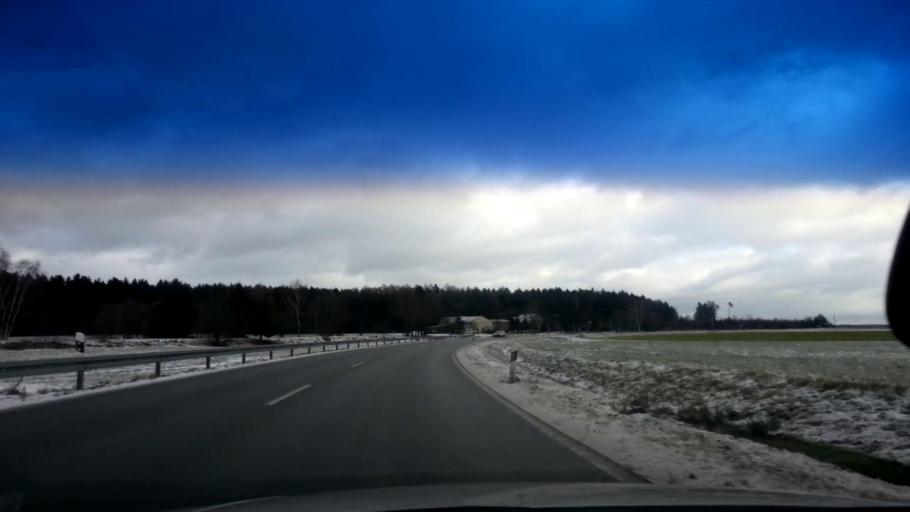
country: DE
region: Bavaria
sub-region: Upper Franconia
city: Weissenstadt
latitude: 50.1203
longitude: 11.9049
